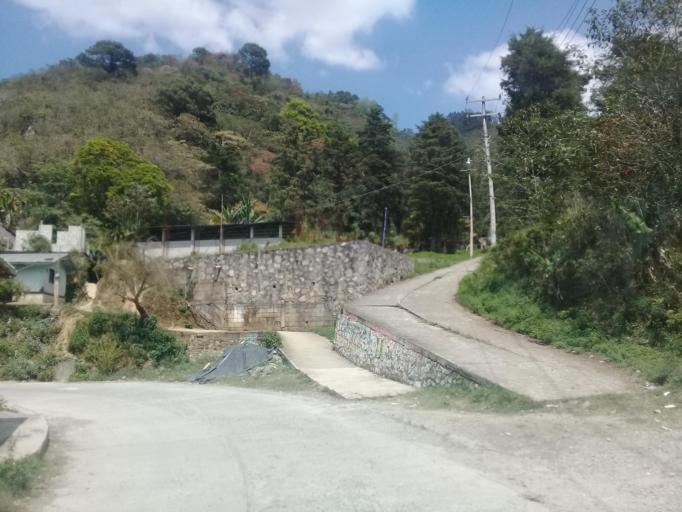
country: MX
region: Veracruz
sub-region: Tlilapan
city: Tonalixco
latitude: 18.7966
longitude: -97.0555
